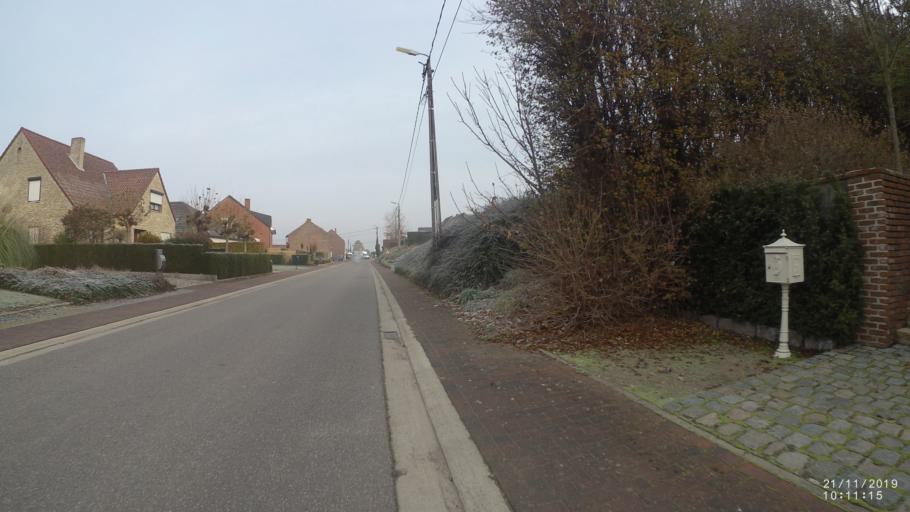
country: BE
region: Flanders
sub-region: Provincie Vlaams-Brabant
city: Zoutleeuw
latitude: 50.8157
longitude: 5.1118
